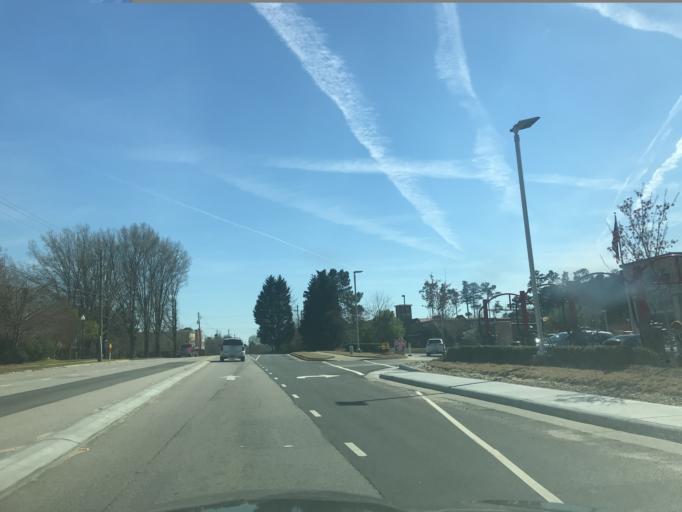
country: US
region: North Carolina
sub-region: Wake County
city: Fuquay-Varina
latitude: 35.5917
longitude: -78.7738
